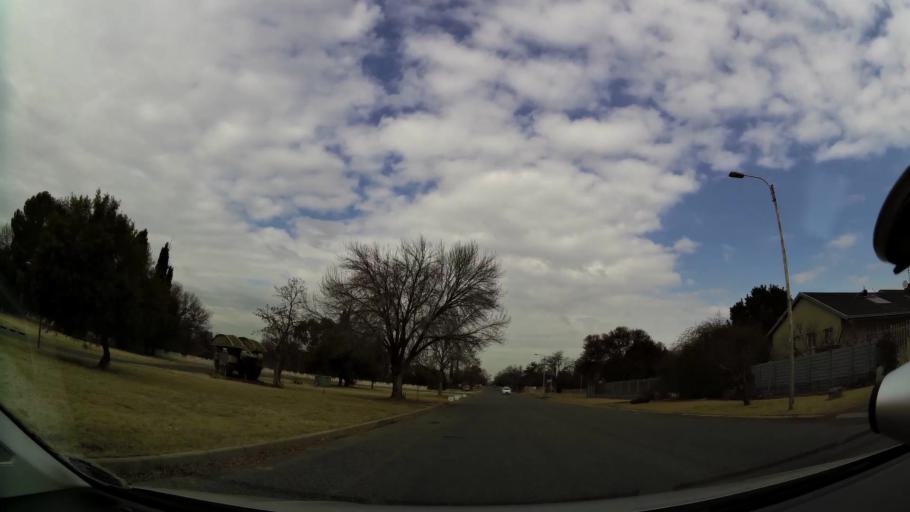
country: ZA
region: Orange Free State
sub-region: Fezile Dabi District Municipality
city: Kroonstad
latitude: -27.6436
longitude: 27.2387
